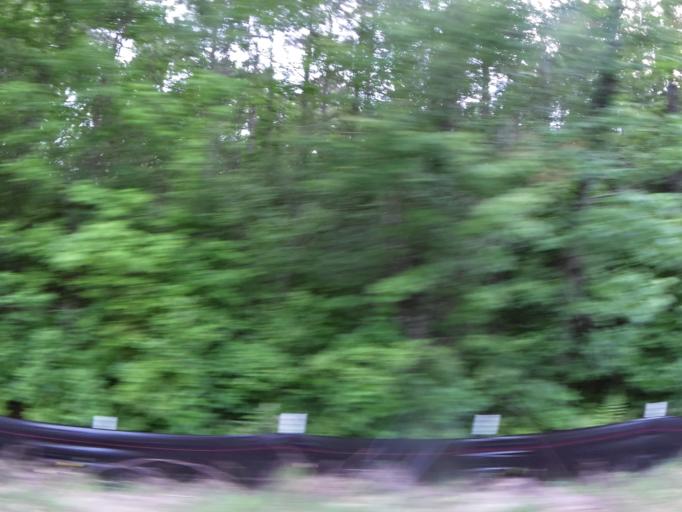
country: US
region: South Carolina
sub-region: Jasper County
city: Ridgeland
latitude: 32.4866
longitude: -81.1203
